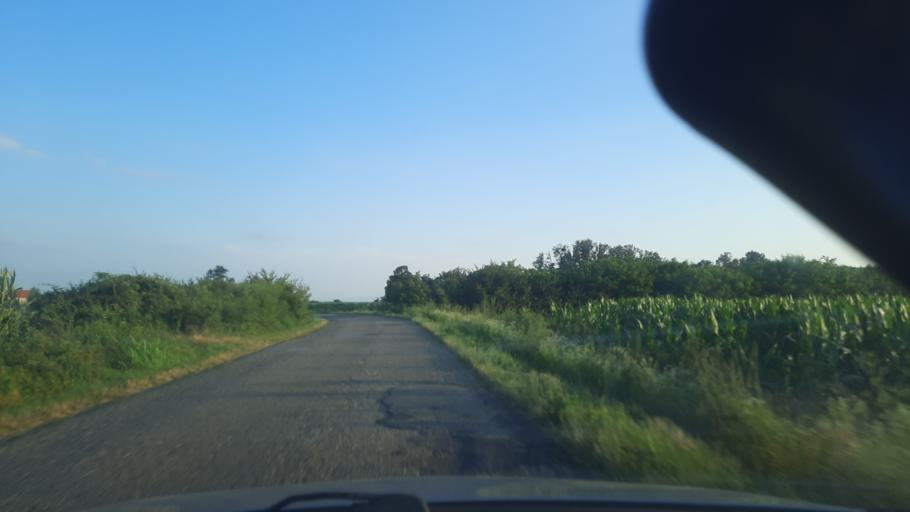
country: RS
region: Central Serbia
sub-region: Macvanski Okrug
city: Vladimirci
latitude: 44.6405
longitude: 19.8396
